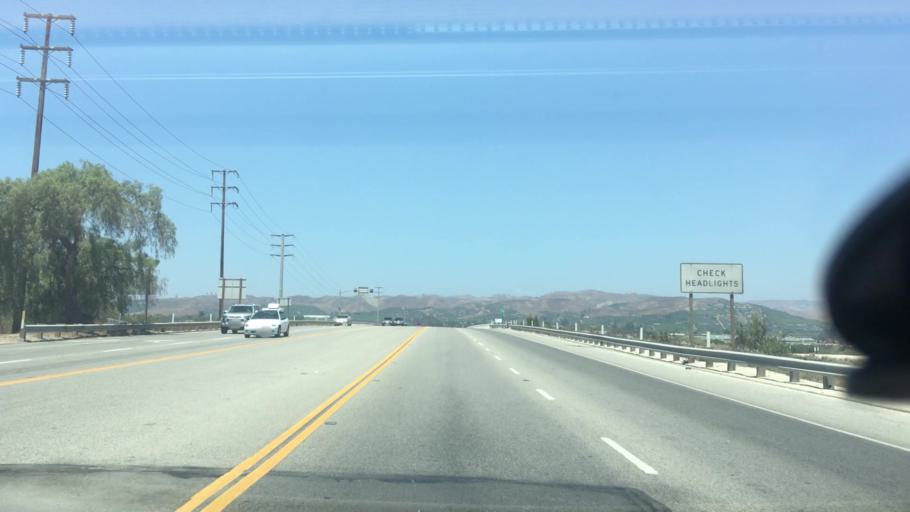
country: US
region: California
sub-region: Ventura County
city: Saticoy
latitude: 34.2745
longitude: -119.1359
